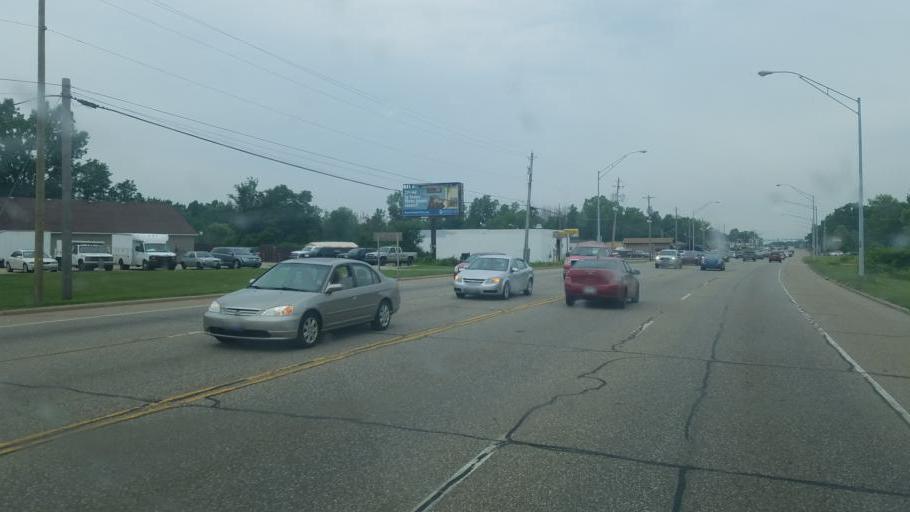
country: US
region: Ohio
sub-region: Summit County
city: Sawyerwood
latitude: 41.0292
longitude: -81.4558
